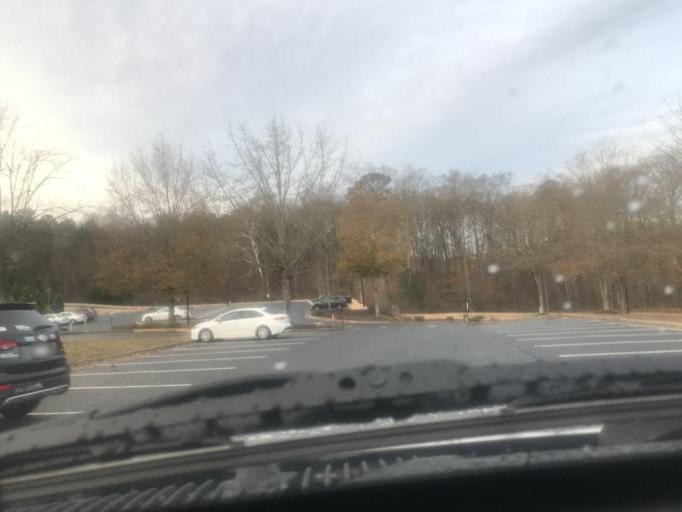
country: US
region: Georgia
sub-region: Gwinnett County
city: Suwanee
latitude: 34.0254
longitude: -84.1018
